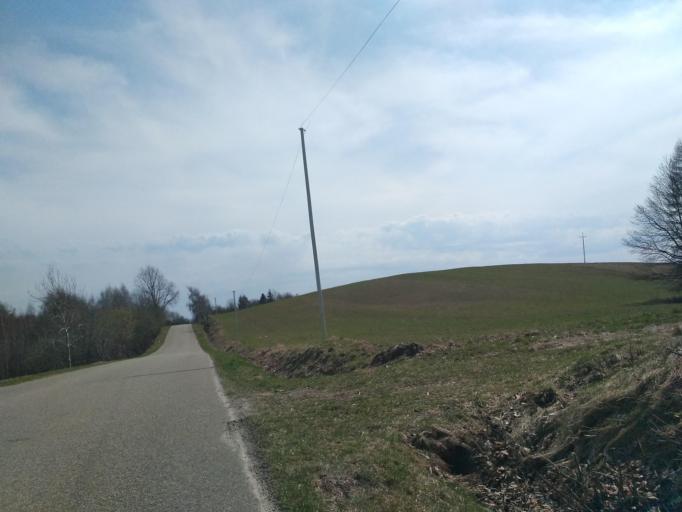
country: PL
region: Subcarpathian Voivodeship
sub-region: Powiat ropczycko-sedziszowski
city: Iwierzyce
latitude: 49.9791
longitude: 21.7441
